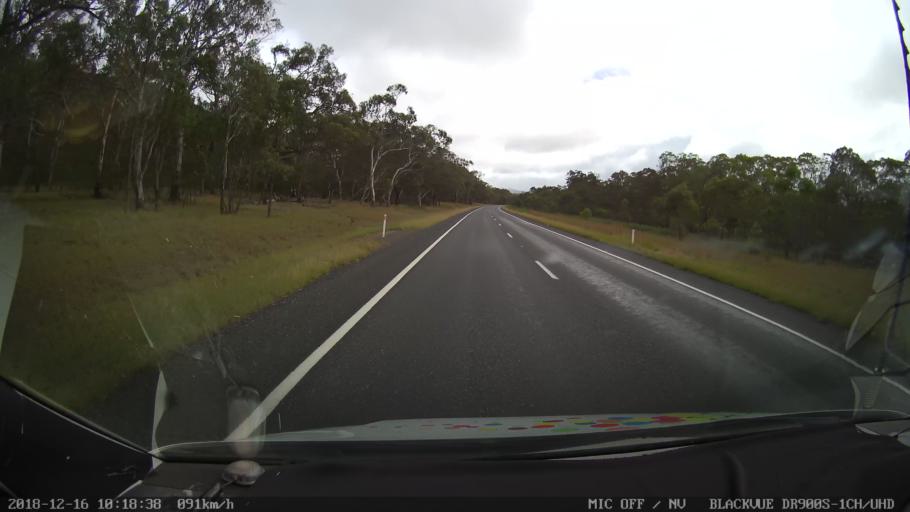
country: AU
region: New South Wales
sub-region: Tenterfield Municipality
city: Carrolls Creek
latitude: -29.2410
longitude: 151.9991
